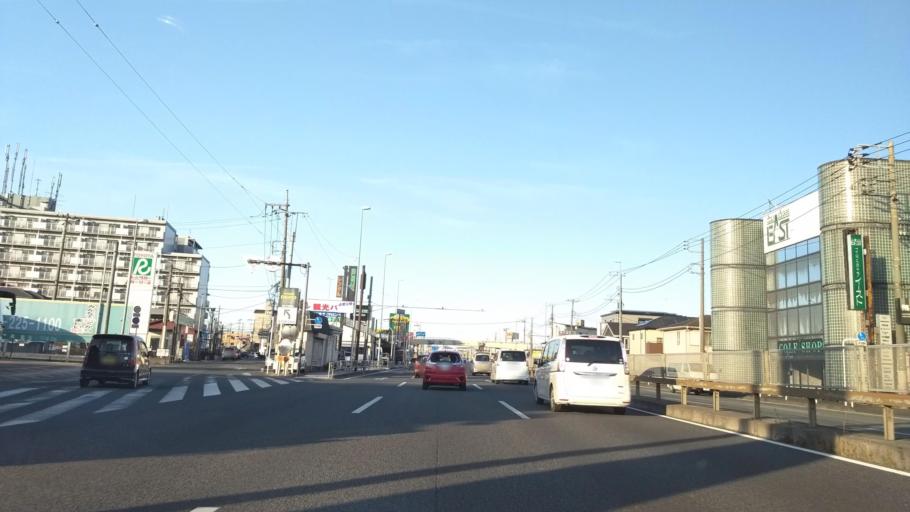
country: JP
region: Kanagawa
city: Atsugi
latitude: 35.4567
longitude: 139.3591
